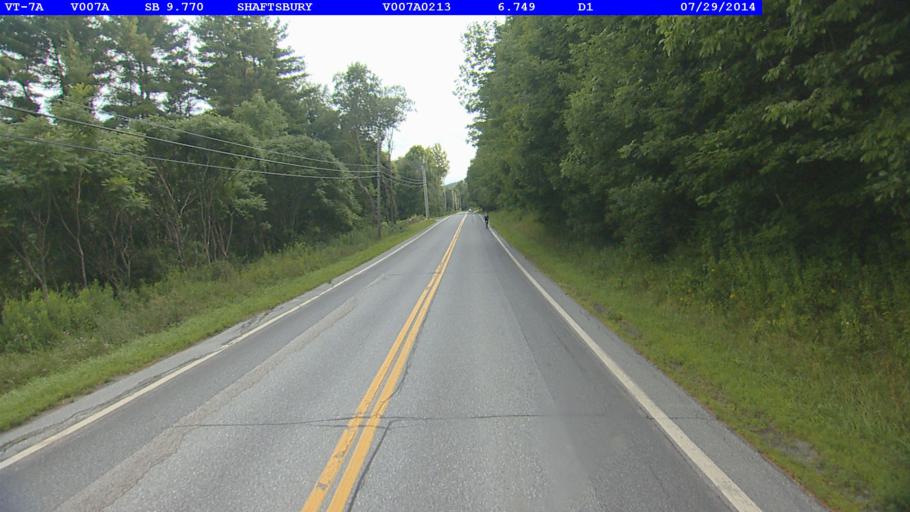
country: US
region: Vermont
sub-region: Bennington County
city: Arlington
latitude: 43.0251
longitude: -73.1863
